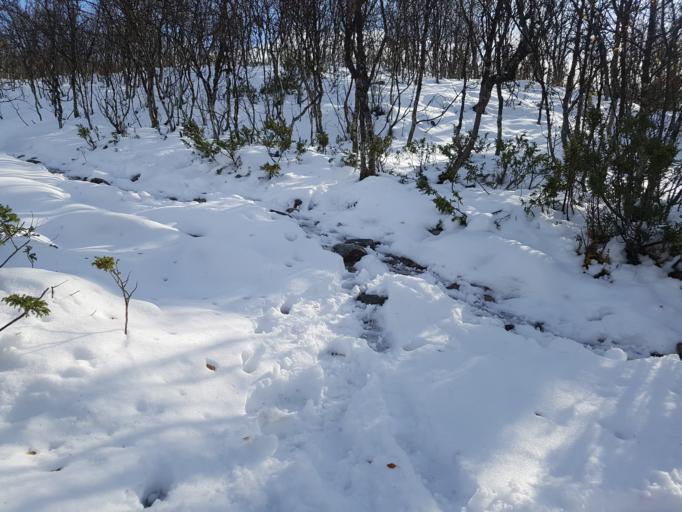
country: NO
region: Oppland
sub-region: Sel
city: Otta
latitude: 61.8268
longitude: 9.6852
